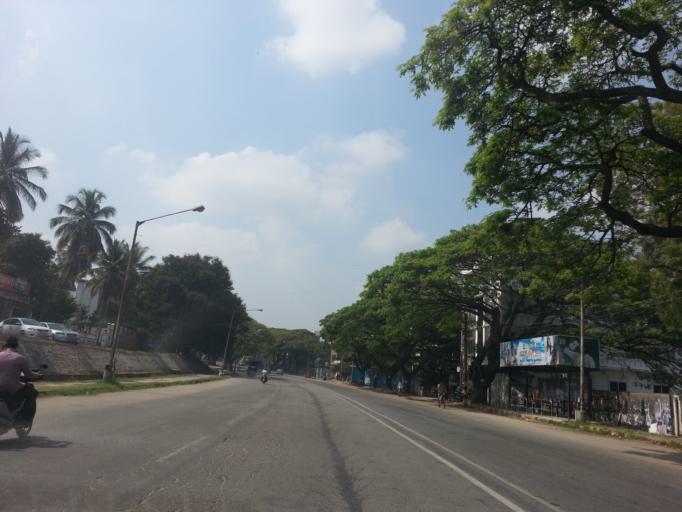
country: IN
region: Karnataka
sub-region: Mysore
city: Mysore
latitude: 12.3299
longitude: 76.6452
